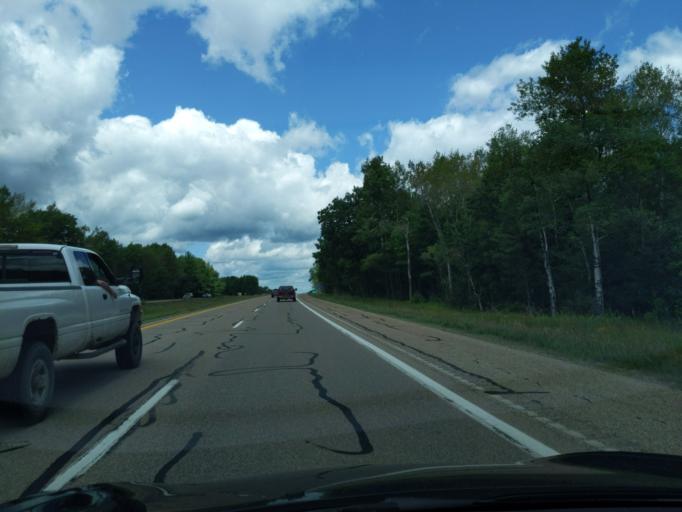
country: US
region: Michigan
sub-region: Roscommon County
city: Houghton Lake
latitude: 44.3246
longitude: -84.8069
